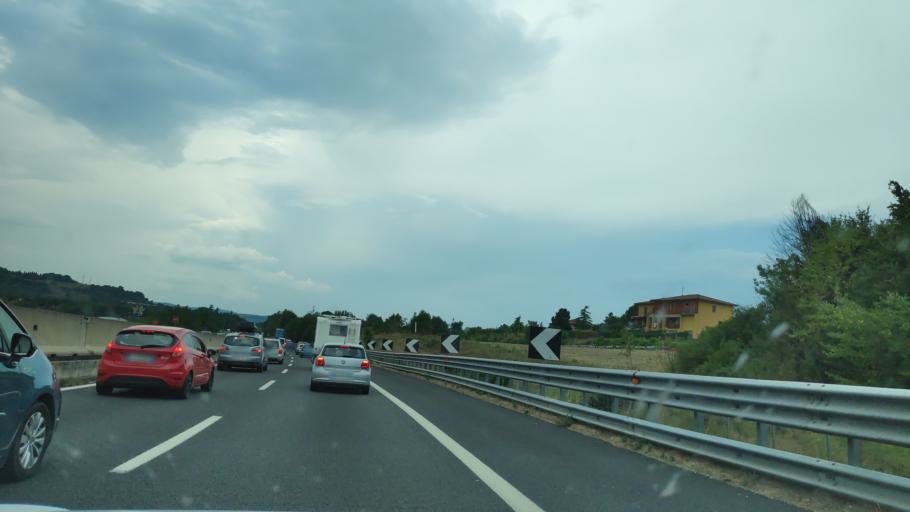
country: IT
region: Tuscany
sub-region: Province of Florence
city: Incisa in Val d'Arno
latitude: 43.6581
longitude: 11.4647
